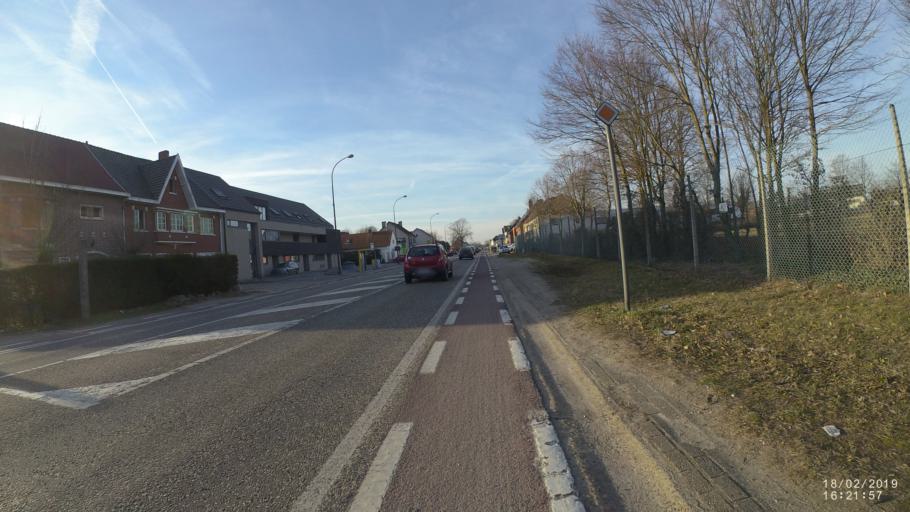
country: BE
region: Flanders
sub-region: Provincie Limburg
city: Zonhoven
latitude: 50.9903
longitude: 5.3474
